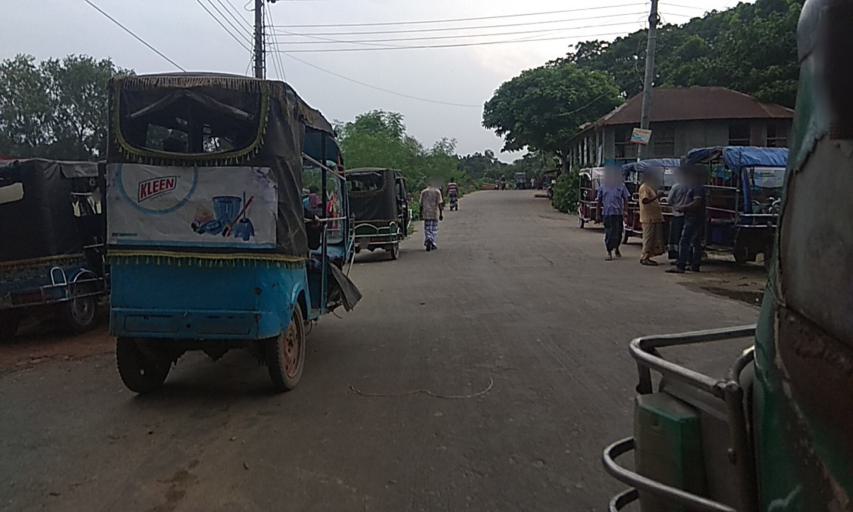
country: BD
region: Dhaka
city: Dohar
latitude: 23.4554
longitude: 90.0076
